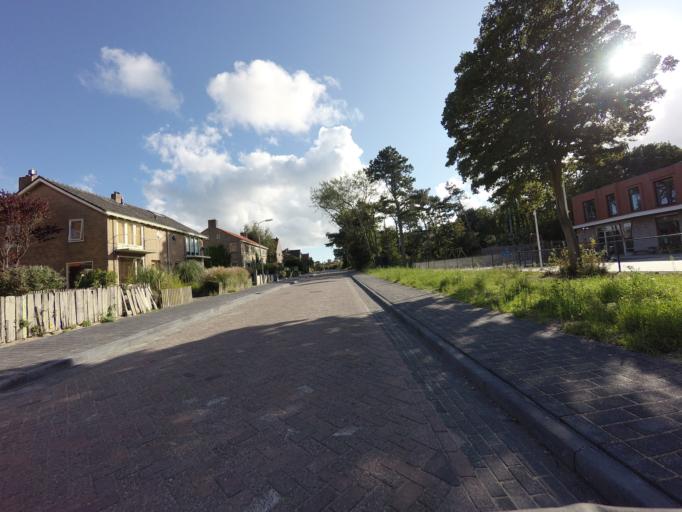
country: NL
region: Friesland
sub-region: Gemeente Terschelling
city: West-Terschelling
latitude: 53.3638
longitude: 5.2146
